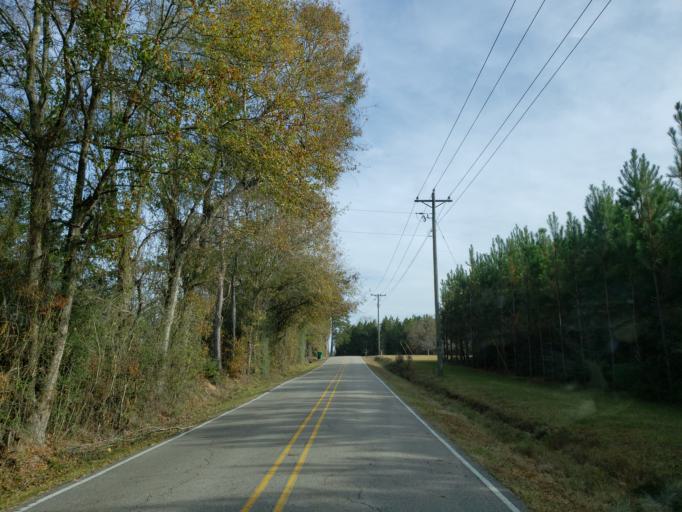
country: US
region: Mississippi
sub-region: Forrest County
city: Rawls Springs
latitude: 31.4151
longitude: -89.4174
